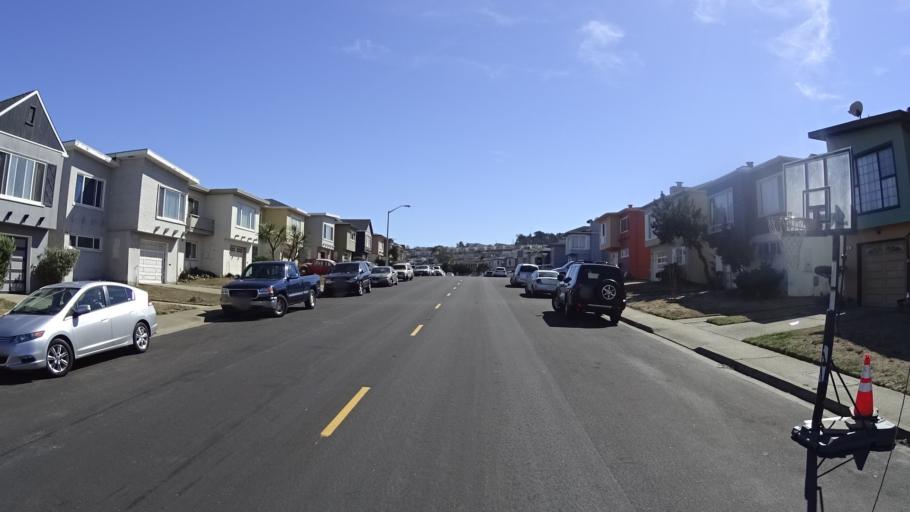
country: US
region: California
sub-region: San Mateo County
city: Broadmoor
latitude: 37.6930
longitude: -122.4954
